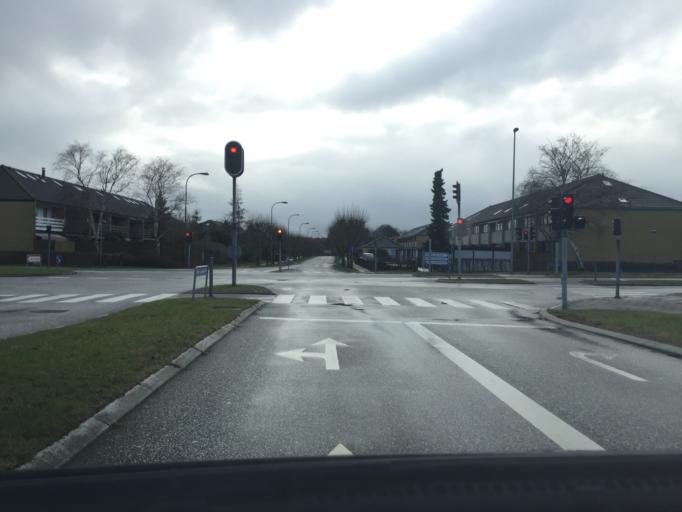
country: DK
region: Capital Region
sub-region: Fureso Kommune
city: Stavnsholt
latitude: 55.8137
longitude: 12.3886
